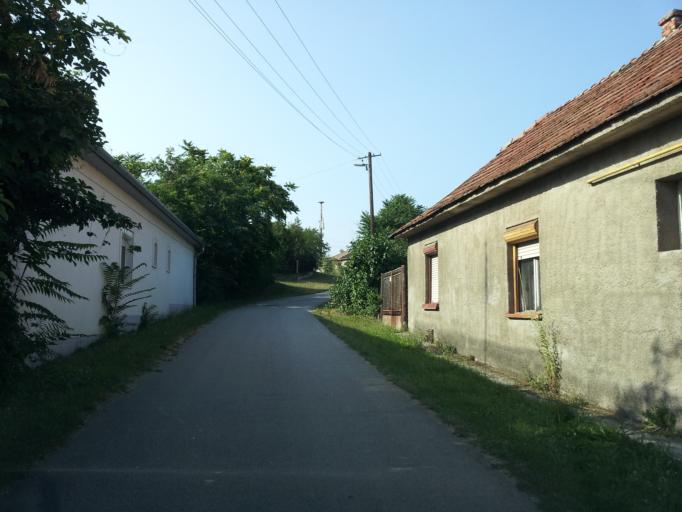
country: HU
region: Veszprem
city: Hajmasker
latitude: 47.1092
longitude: 18.0598
